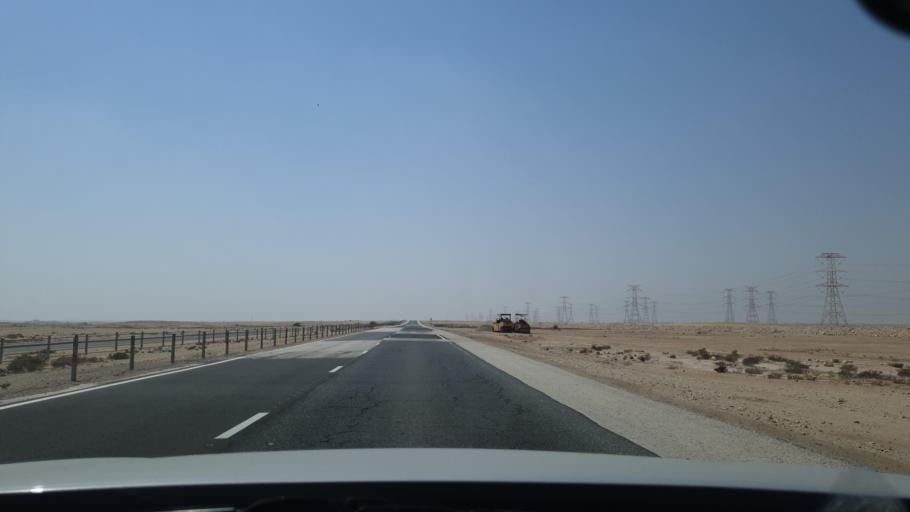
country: QA
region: Al Khawr
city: Al Khawr
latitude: 25.7283
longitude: 51.4556
